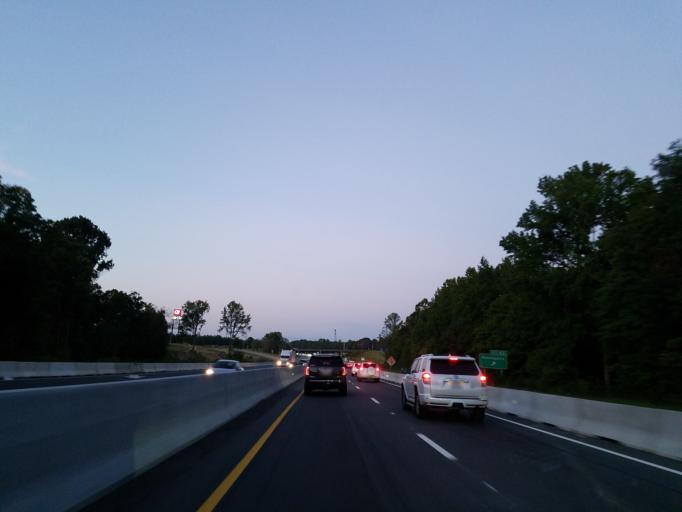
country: US
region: North Carolina
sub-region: Cabarrus County
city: Kannapolis
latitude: 35.4936
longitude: -80.5675
